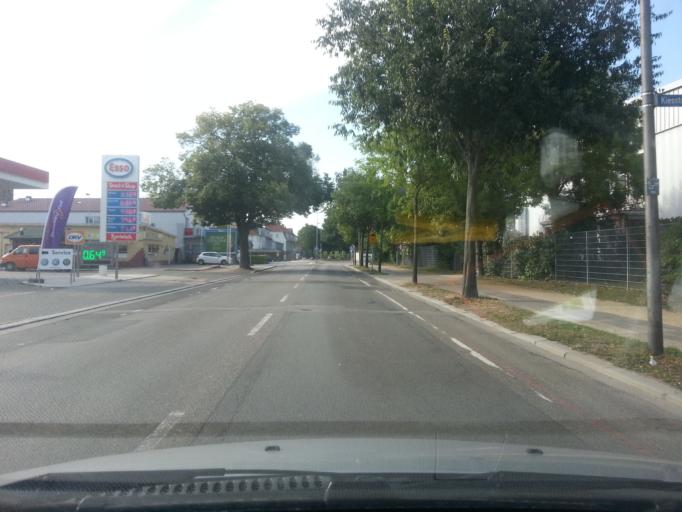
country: DE
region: Rheinland-Pfalz
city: Worms
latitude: 49.6431
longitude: 8.3630
